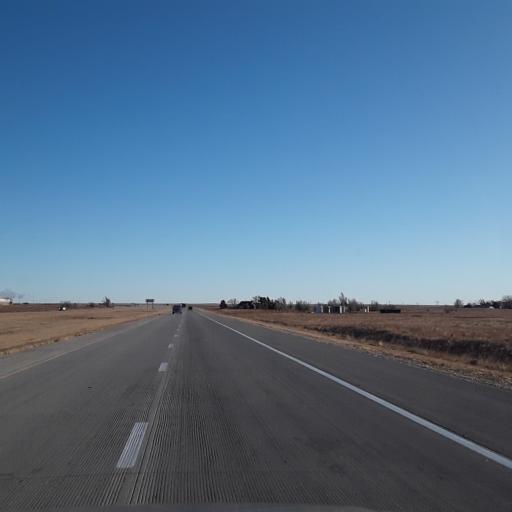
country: US
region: Kansas
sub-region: Seward County
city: Liberal
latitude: 37.0959
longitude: -100.8109
